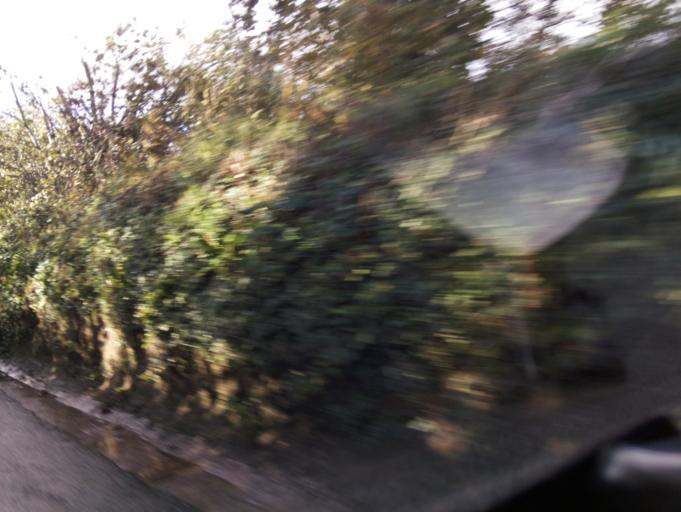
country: GB
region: England
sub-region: Devon
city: Totnes
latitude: 50.3602
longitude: -3.7325
